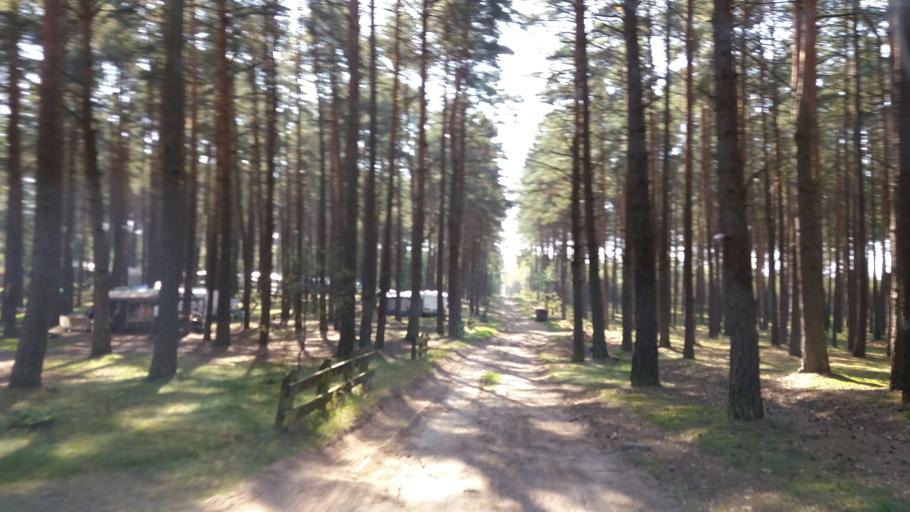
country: PL
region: West Pomeranian Voivodeship
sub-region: Powiat drawski
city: Kalisz Pomorski
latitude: 53.2240
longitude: 15.9029
